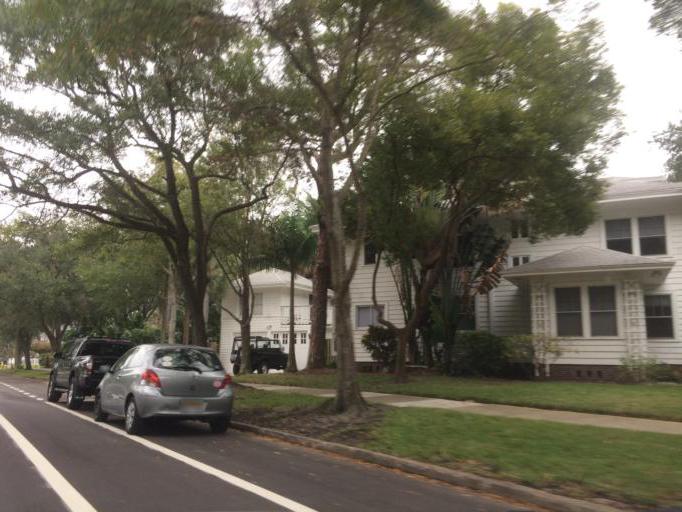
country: US
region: Florida
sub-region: Pinellas County
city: Saint Petersburg
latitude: 27.7857
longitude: -82.6261
